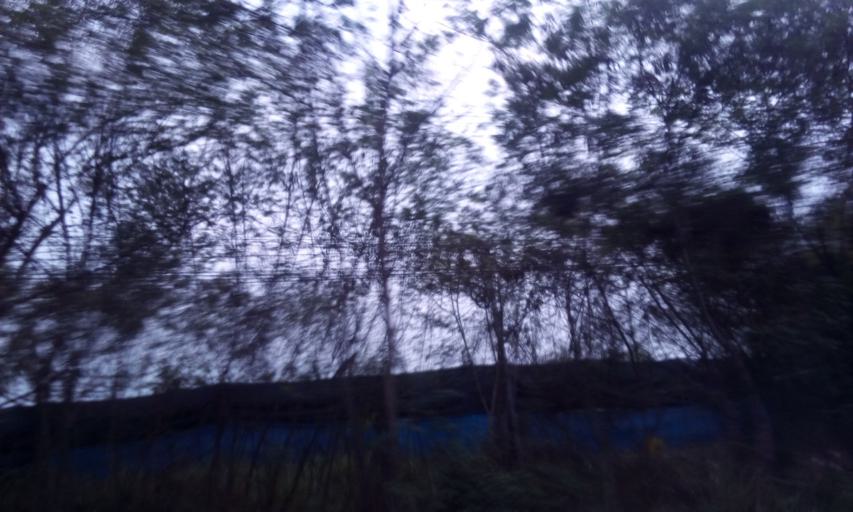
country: TH
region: Chachoengsao
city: Plaeng Yao
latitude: 13.4914
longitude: 101.2751
